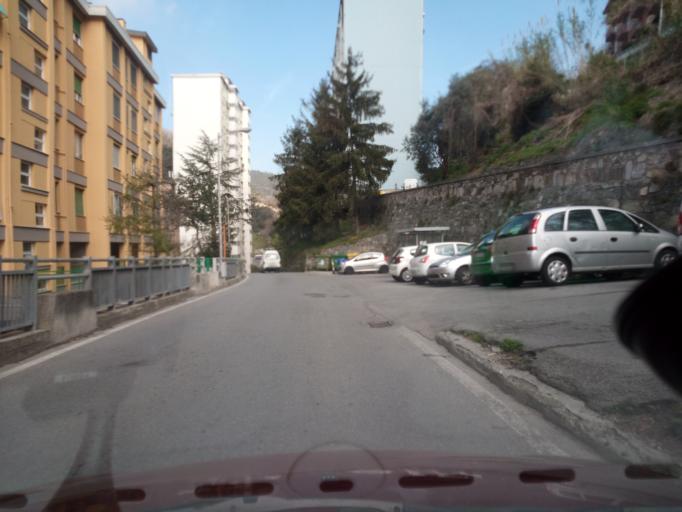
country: IT
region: Liguria
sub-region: Provincia di Genova
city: Mele
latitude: 44.4320
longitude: 8.7790
